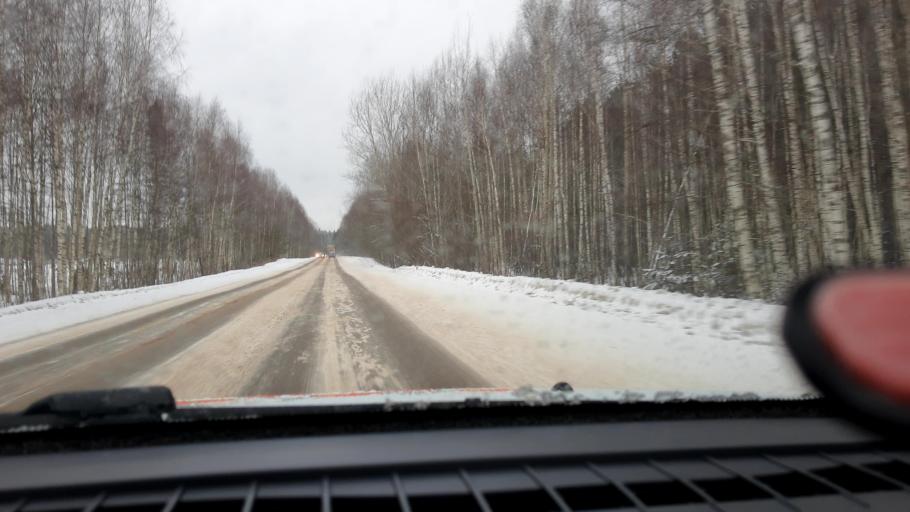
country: RU
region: Nizjnij Novgorod
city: Pamyat' Parizhskoy Kommuny
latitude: 56.2751
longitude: 44.3999
